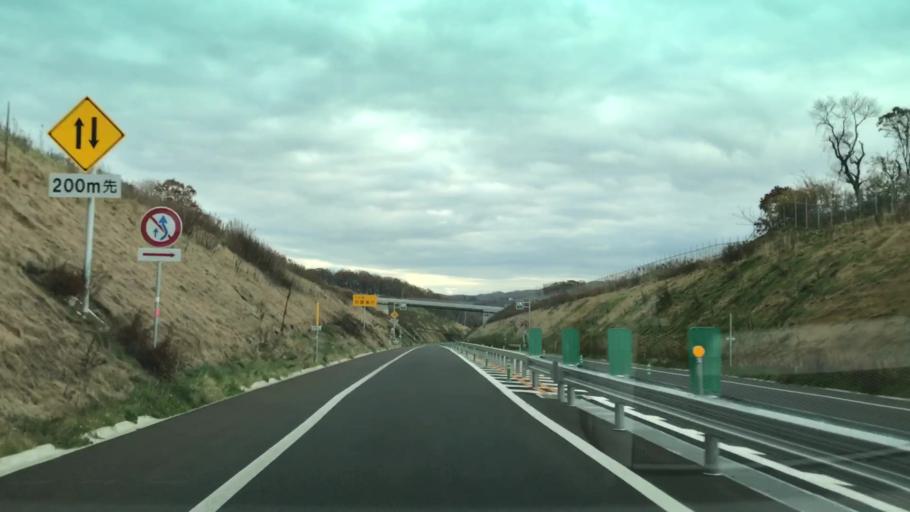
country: JP
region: Hokkaido
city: Shizunai-furukawacho
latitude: 42.4580
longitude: 142.1885
